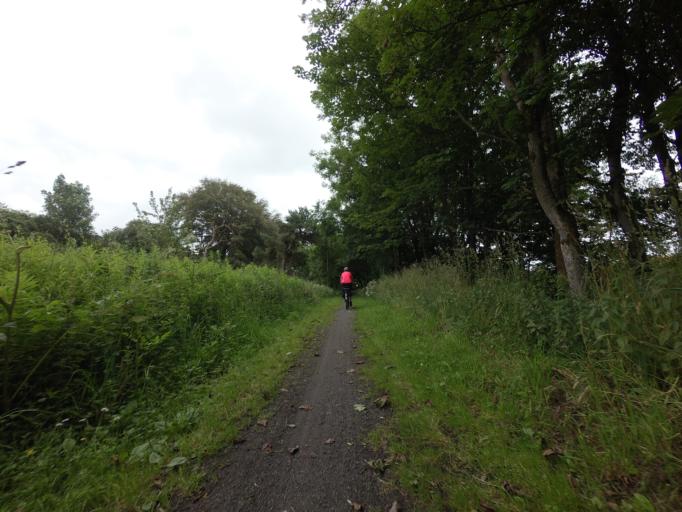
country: GB
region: Scotland
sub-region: Aberdeenshire
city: Ellon
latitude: 57.4762
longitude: -2.1283
